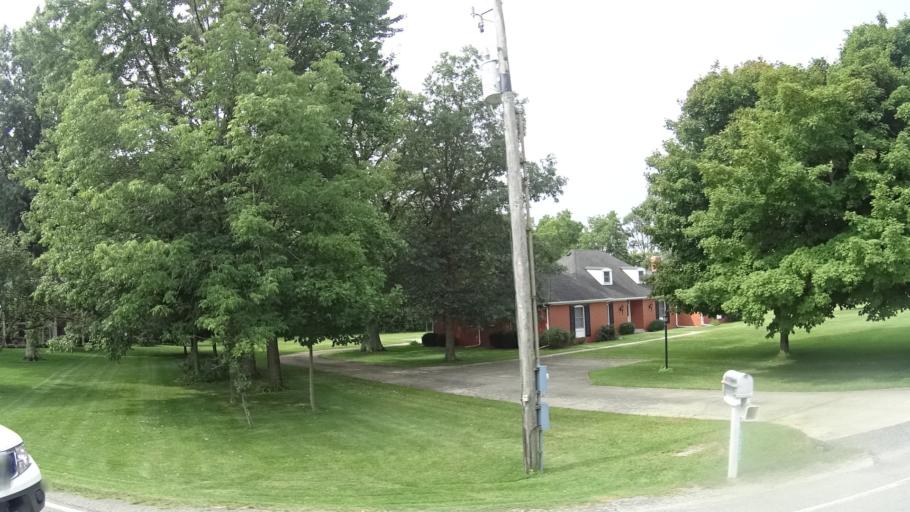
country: US
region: Indiana
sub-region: Madison County
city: Pendleton
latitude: 40.0211
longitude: -85.7717
